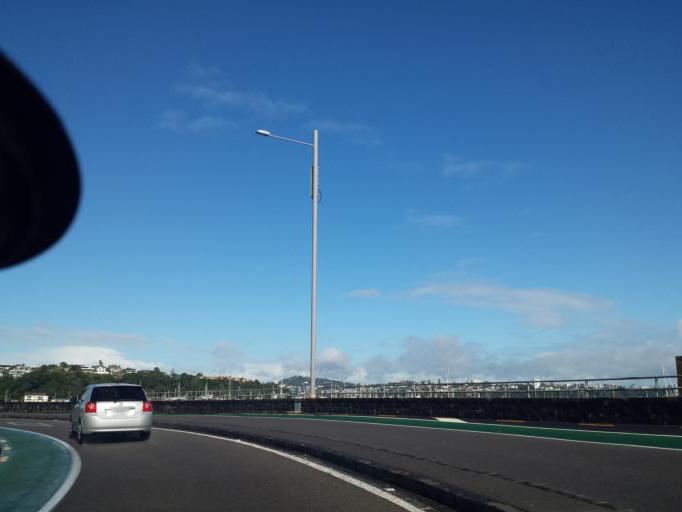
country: NZ
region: Auckland
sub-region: Auckland
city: Auckland
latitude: -36.8455
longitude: 174.8173
